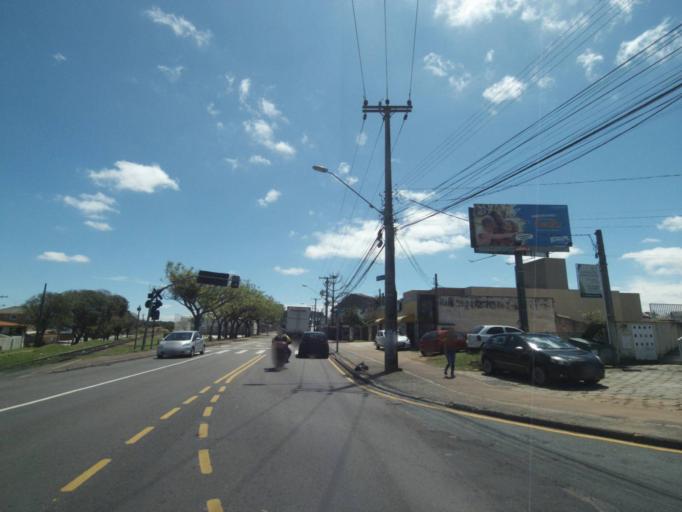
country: BR
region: Parana
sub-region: Curitiba
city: Curitiba
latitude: -25.3842
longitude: -49.2617
